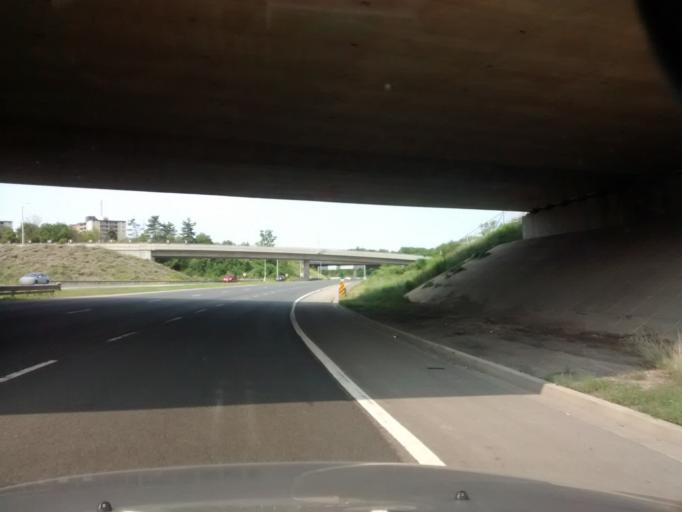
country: CA
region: Ontario
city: Hamilton
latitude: 43.2265
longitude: -79.7899
